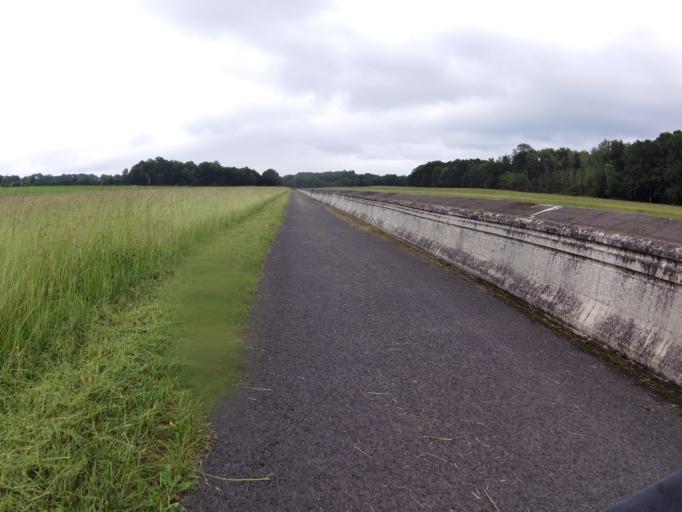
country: FR
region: Champagne-Ardenne
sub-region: Departement de la Haute-Marne
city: Villiers-en-Lieu
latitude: 48.6144
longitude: 4.8753
